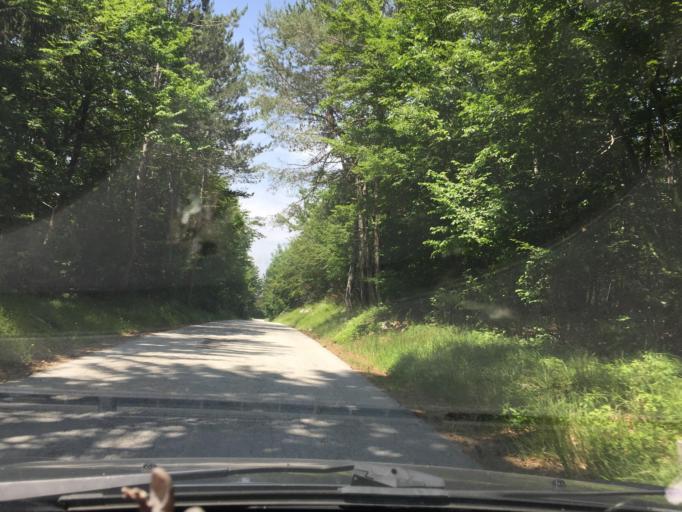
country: HR
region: Istarska
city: Buzet
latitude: 45.4758
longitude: 14.0797
